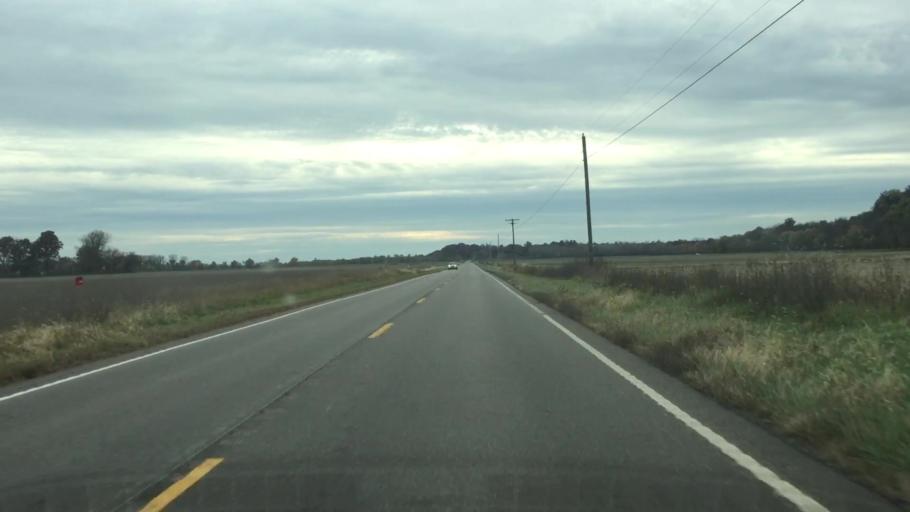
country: US
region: Missouri
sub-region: Callaway County
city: Fulton
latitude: 38.7042
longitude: -91.8040
